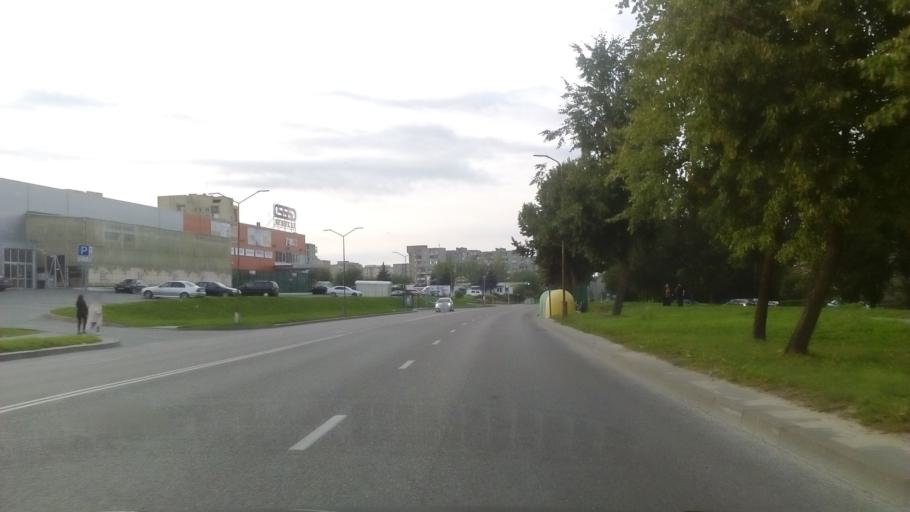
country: LT
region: Alytaus apskritis
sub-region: Alytus
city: Alytus
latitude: 54.3923
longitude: 24.0197
